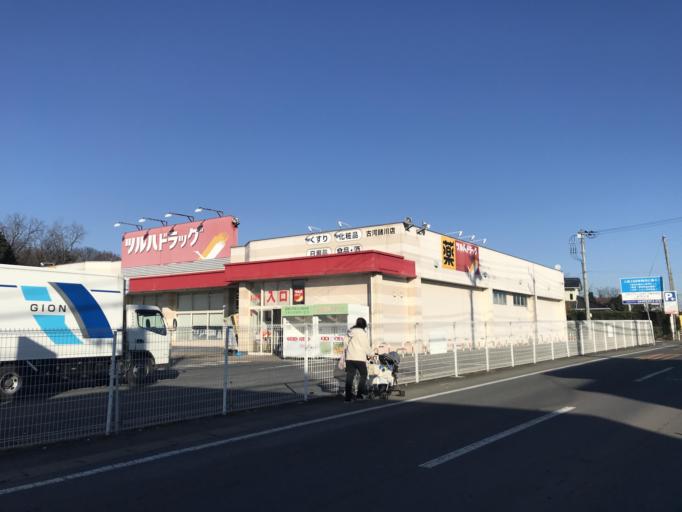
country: JP
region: Ibaraki
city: Koga
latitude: 36.2018
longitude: 139.8082
